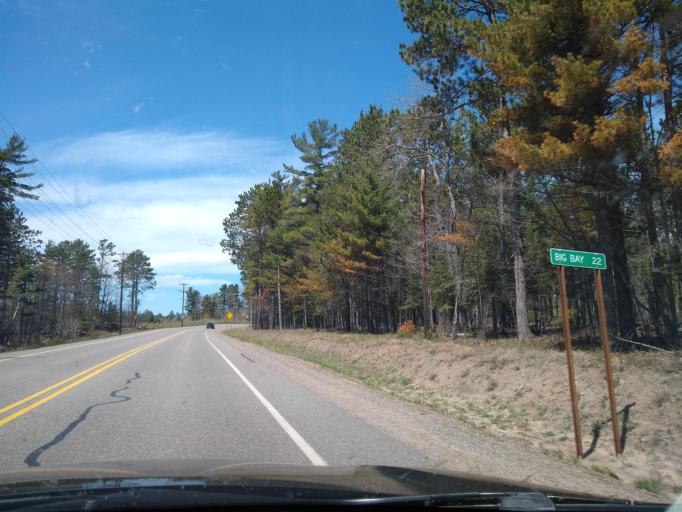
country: US
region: Michigan
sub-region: Marquette County
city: Trowbridge Park
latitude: 46.5922
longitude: -87.4510
